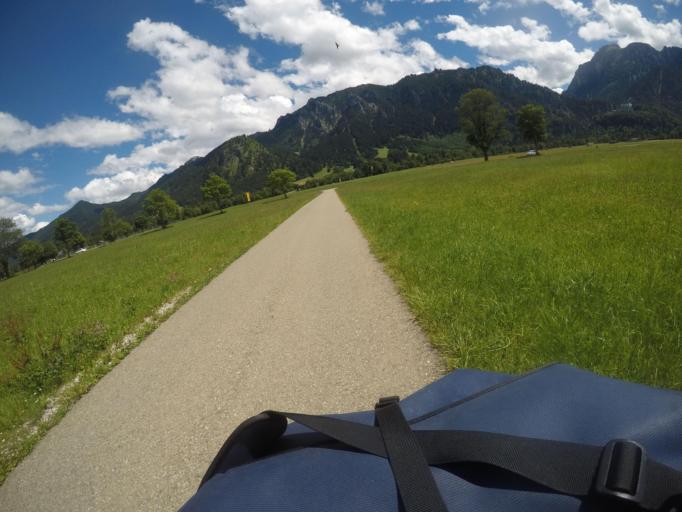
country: DE
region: Bavaria
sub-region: Swabia
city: Schwangau
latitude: 47.5736
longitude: 10.7455
